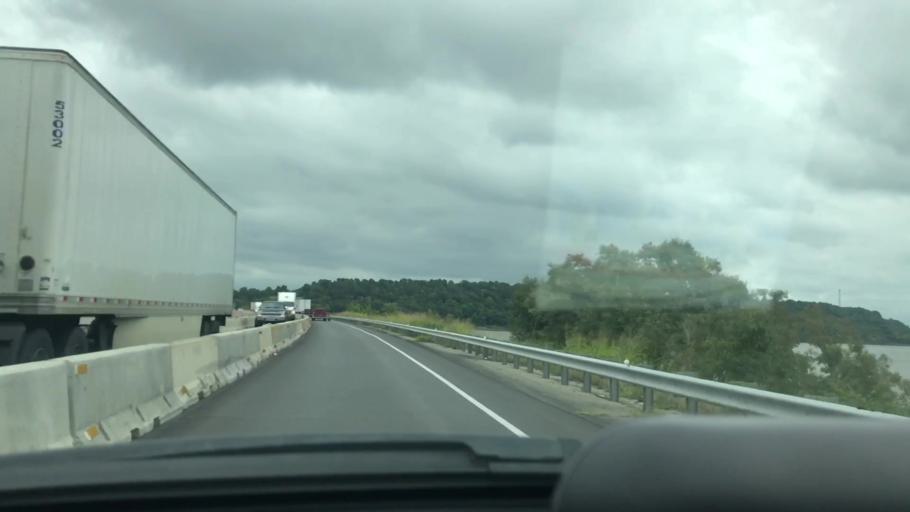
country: US
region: Oklahoma
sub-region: McIntosh County
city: Eufaula
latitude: 35.2412
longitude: -95.5872
